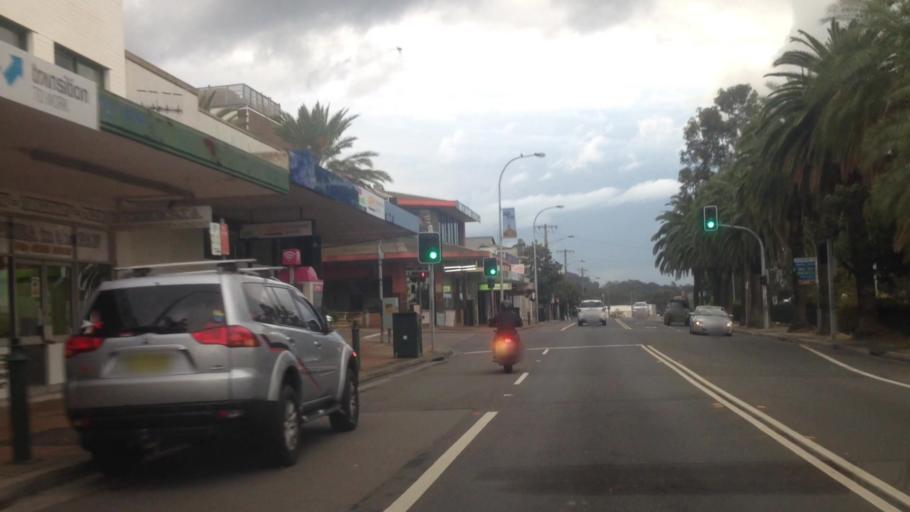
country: AU
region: New South Wales
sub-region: Wyong Shire
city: Chittaway Bay
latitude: -33.2847
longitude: 151.4248
